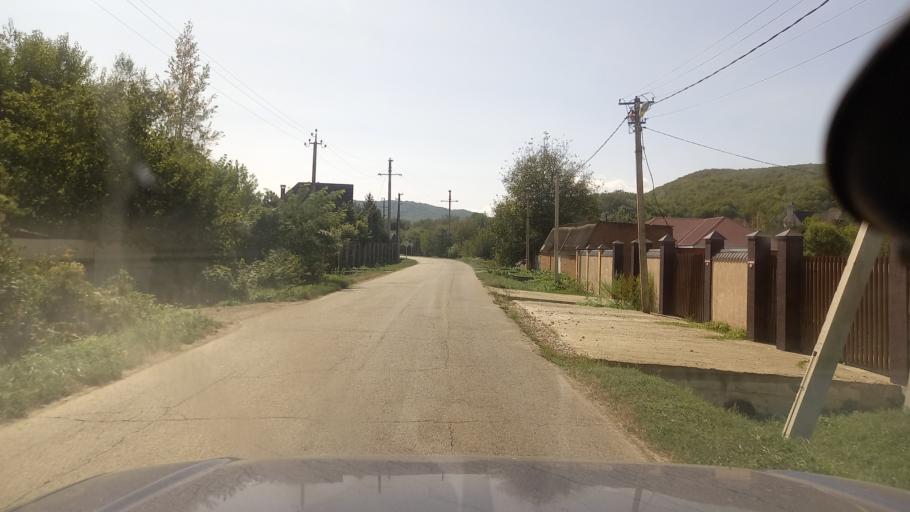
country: RU
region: Krasnodarskiy
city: Azovskaya
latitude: 44.7071
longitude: 38.6722
